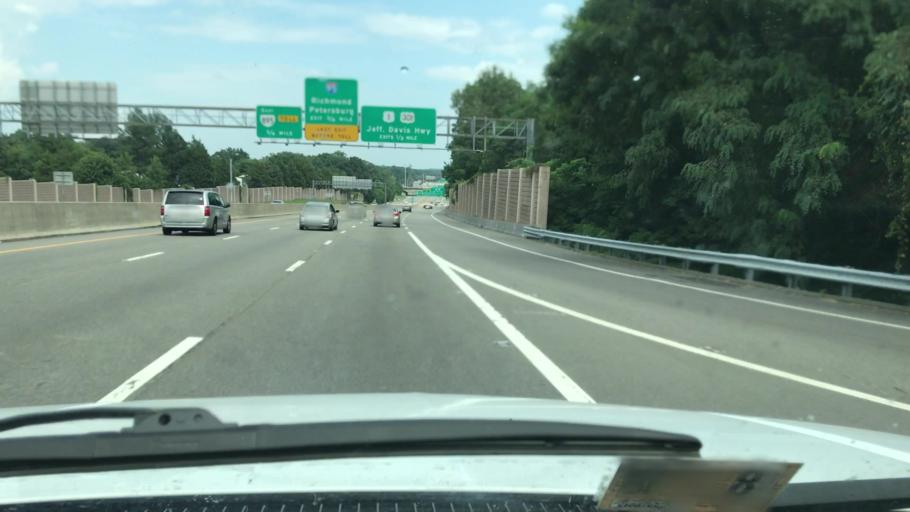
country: US
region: Virginia
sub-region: Chesterfield County
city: Bensley
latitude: 37.4425
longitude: -77.4491
